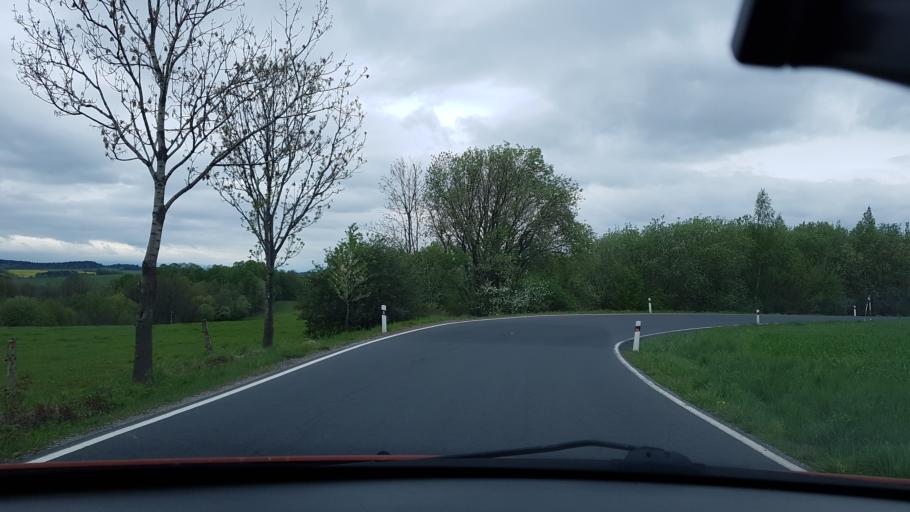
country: CZ
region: Olomoucky
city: Mikulovice
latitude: 50.3116
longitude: 17.2990
